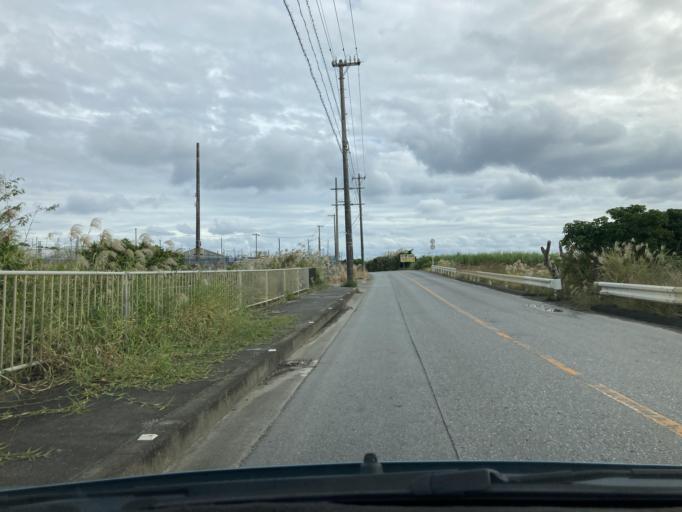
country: JP
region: Okinawa
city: Itoman
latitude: 26.1149
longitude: 127.6979
